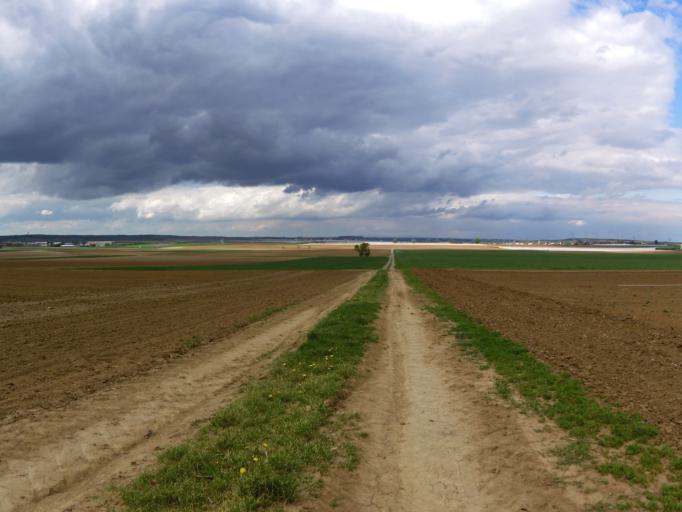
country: DE
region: Bavaria
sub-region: Regierungsbezirk Unterfranken
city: Oberpleichfeld
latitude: 49.8563
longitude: 10.0799
